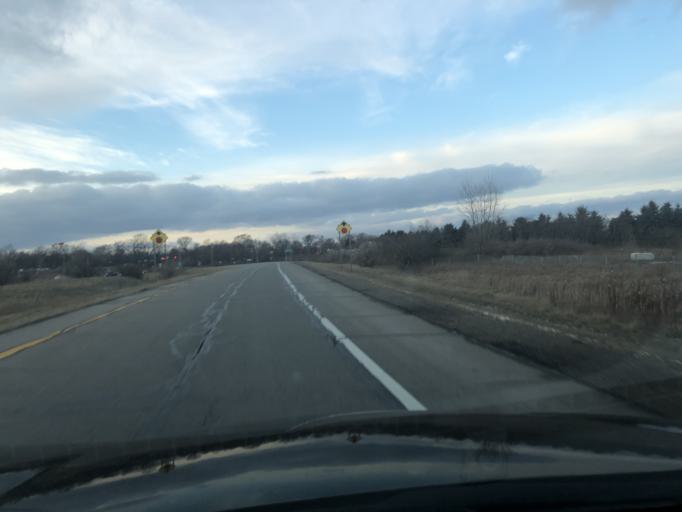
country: US
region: Michigan
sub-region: Oakland County
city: South Lyon
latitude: 42.5190
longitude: -83.6137
